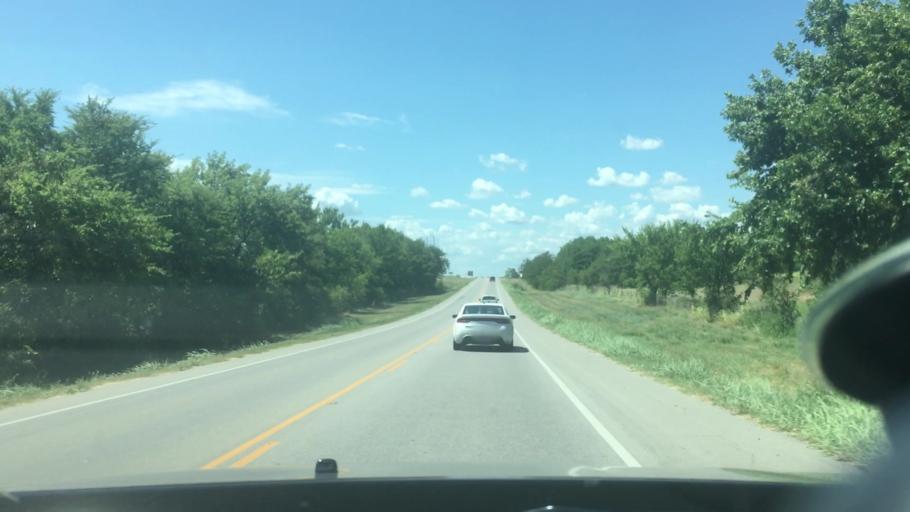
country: US
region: Oklahoma
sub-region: Marshall County
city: Kingston
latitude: 34.0378
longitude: -96.7331
